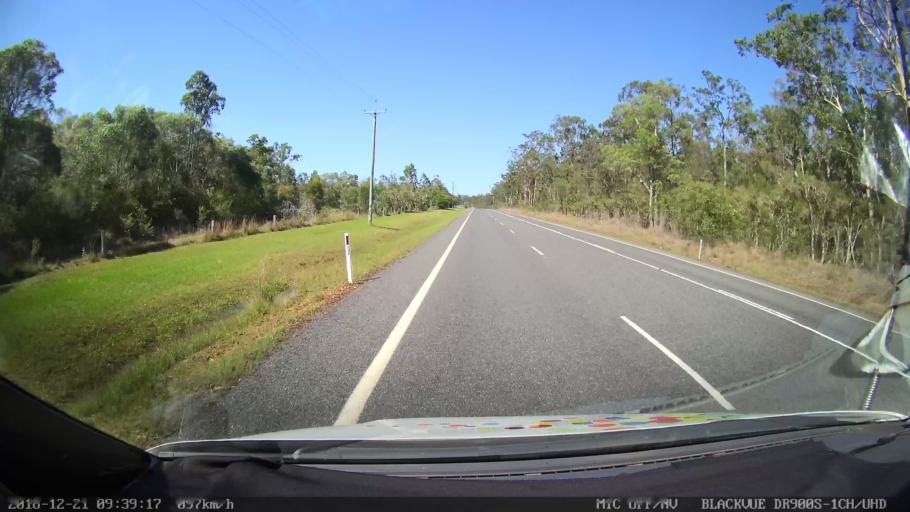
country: AU
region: New South Wales
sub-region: Clarence Valley
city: Grafton
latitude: -29.5594
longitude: 152.9743
